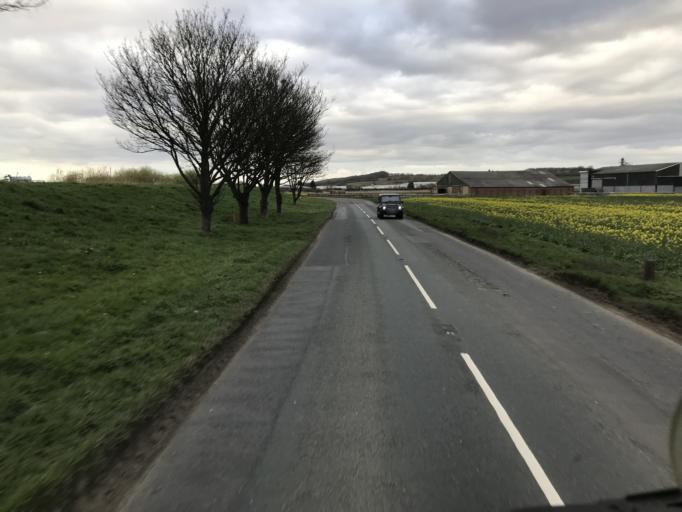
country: GB
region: England
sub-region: North Lincolnshire
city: Gunness
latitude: 53.6116
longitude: -0.6980
